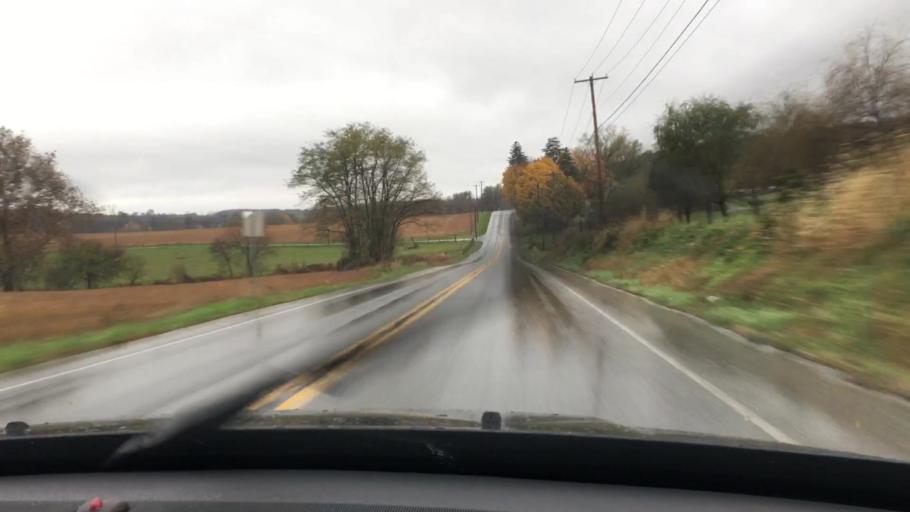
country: US
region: Pennsylvania
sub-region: Lancaster County
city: Quarryville
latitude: 39.8695
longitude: -76.2453
